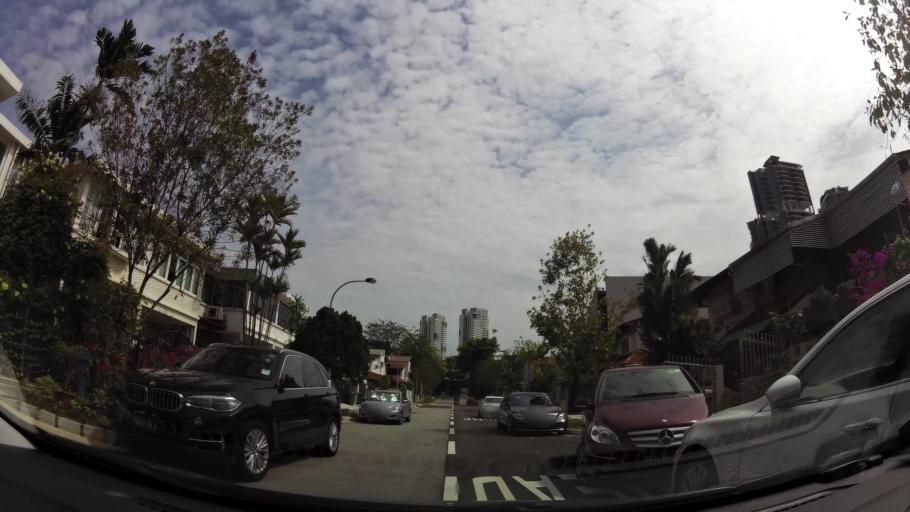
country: SG
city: Singapore
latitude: 1.3188
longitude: 103.7586
